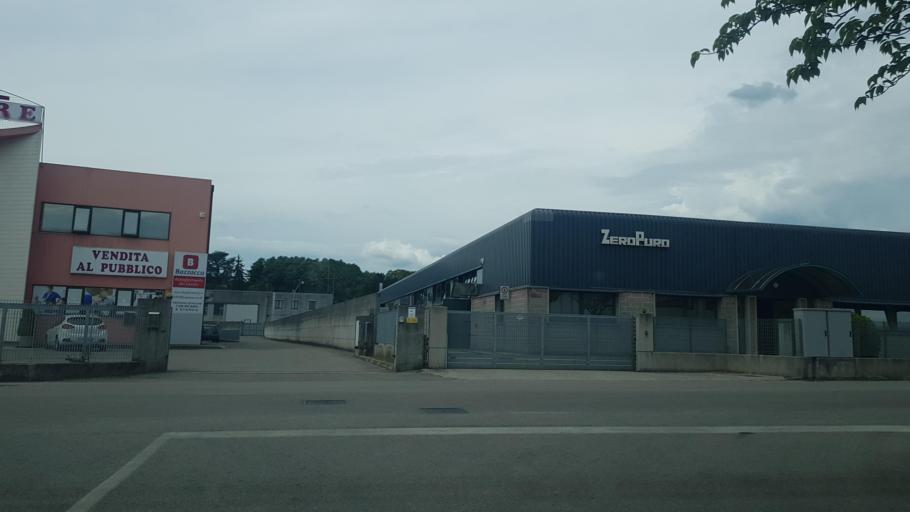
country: IT
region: Veneto
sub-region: Provincia di Treviso
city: Cornuda
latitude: 45.8365
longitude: 12.0145
